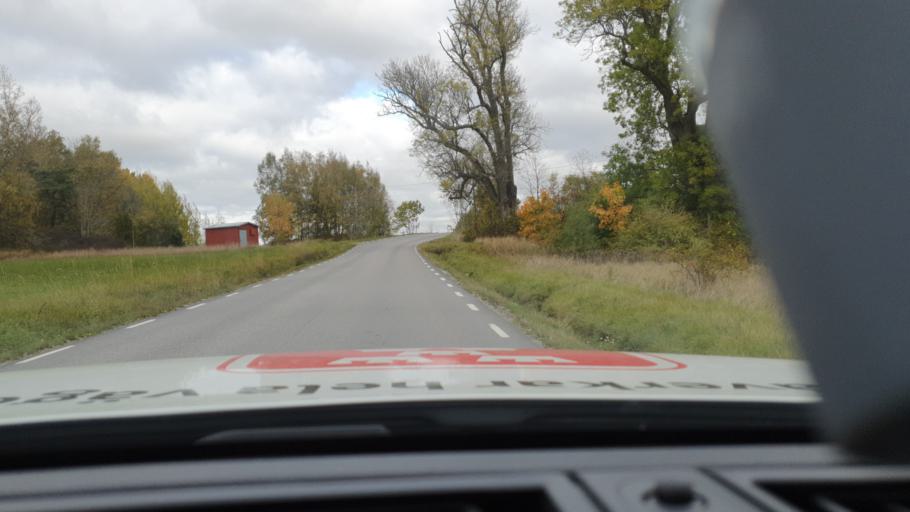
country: SE
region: Stockholm
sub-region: Upplands-Bro Kommun
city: Bro
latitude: 59.5062
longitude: 17.5768
